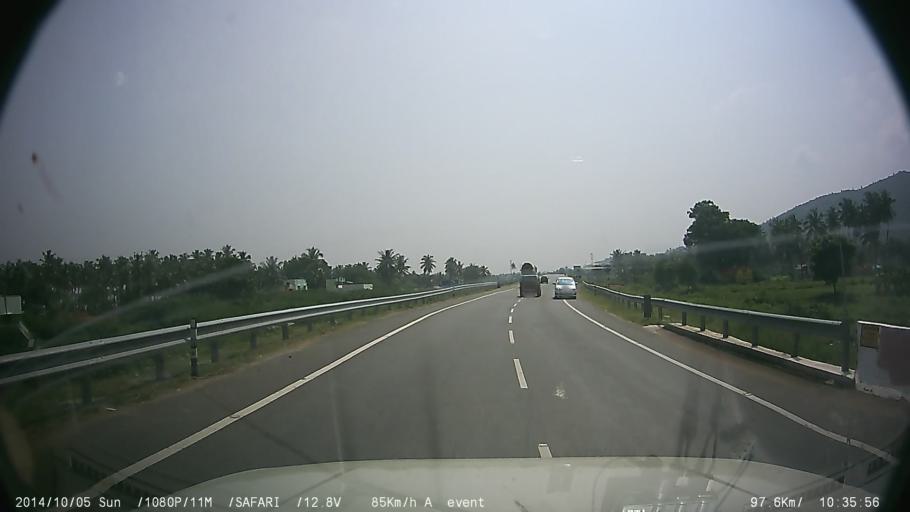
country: IN
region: Tamil Nadu
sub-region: Salem
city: Salem
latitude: 11.6611
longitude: 78.2107
